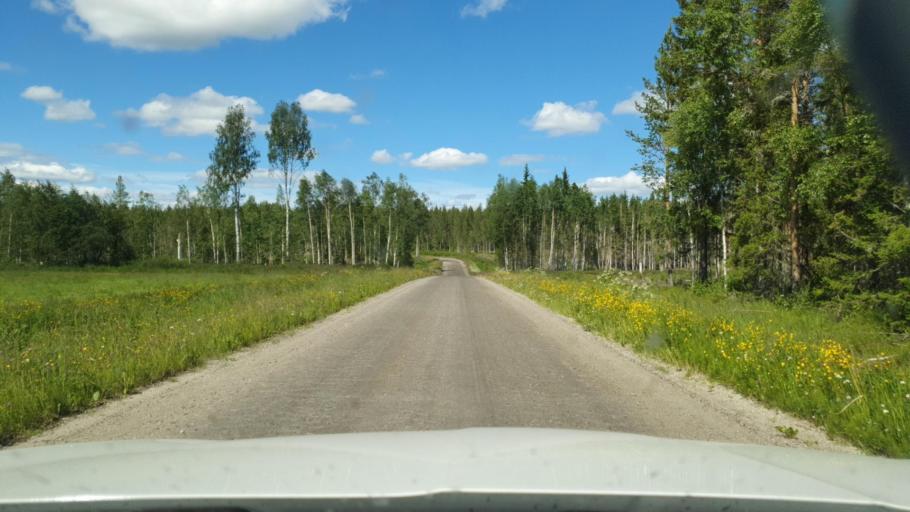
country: SE
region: Norrbotten
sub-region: Pitea Kommun
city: Roknas
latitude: 65.1585
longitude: 21.1569
